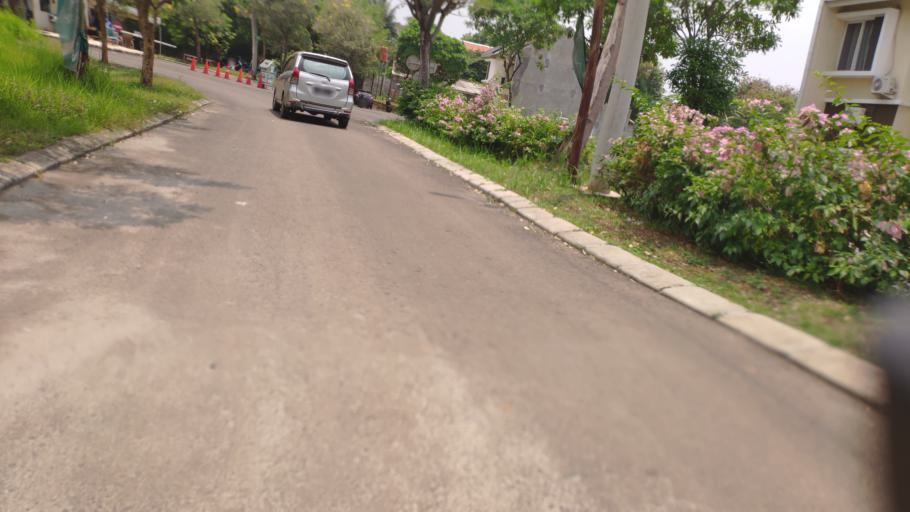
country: ID
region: West Java
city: Sawangan
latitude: -6.3894
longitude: 106.7928
